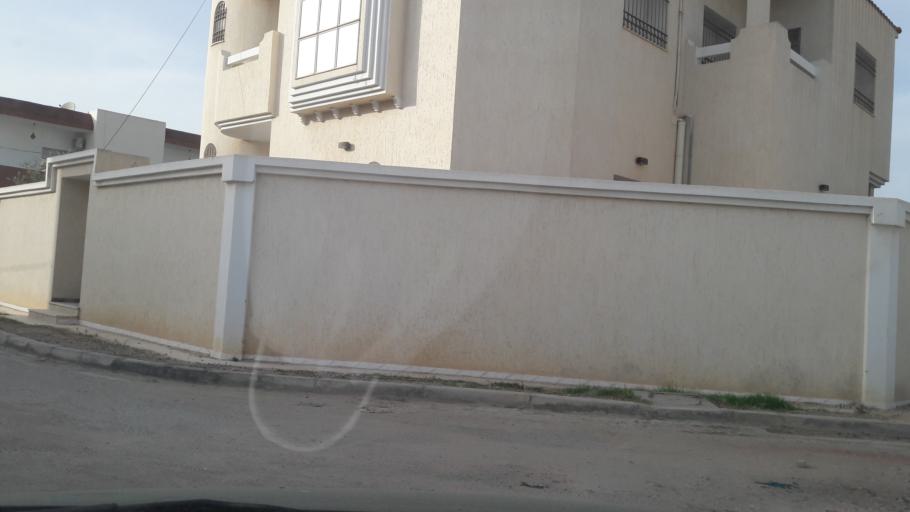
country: TN
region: Safaqis
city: Al Qarmadah
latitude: 34.7990
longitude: 10.7544
